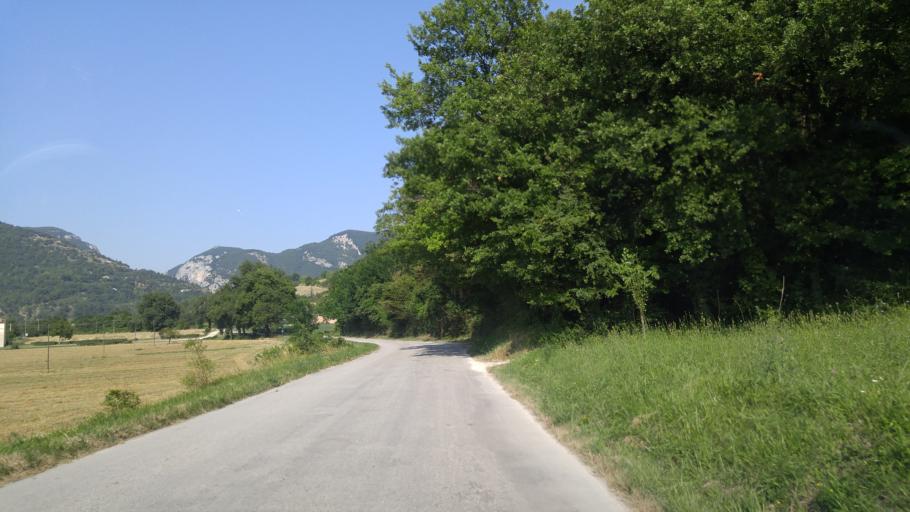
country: IT
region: The Marches
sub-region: Provincia di Pesaro e Urbino
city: Acqualagna
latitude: 43.6294
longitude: 12.6893
